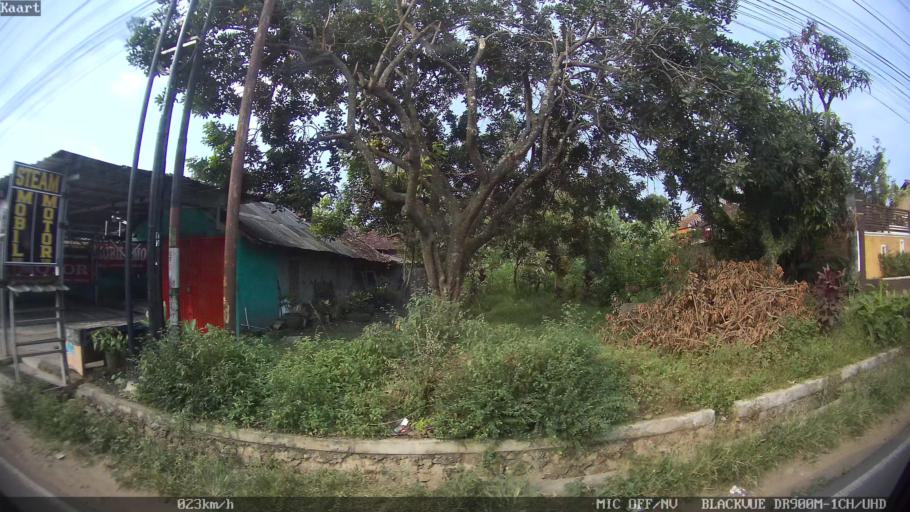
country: ID
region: Lampung
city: Natar
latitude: -5.3675
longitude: 105.1898
